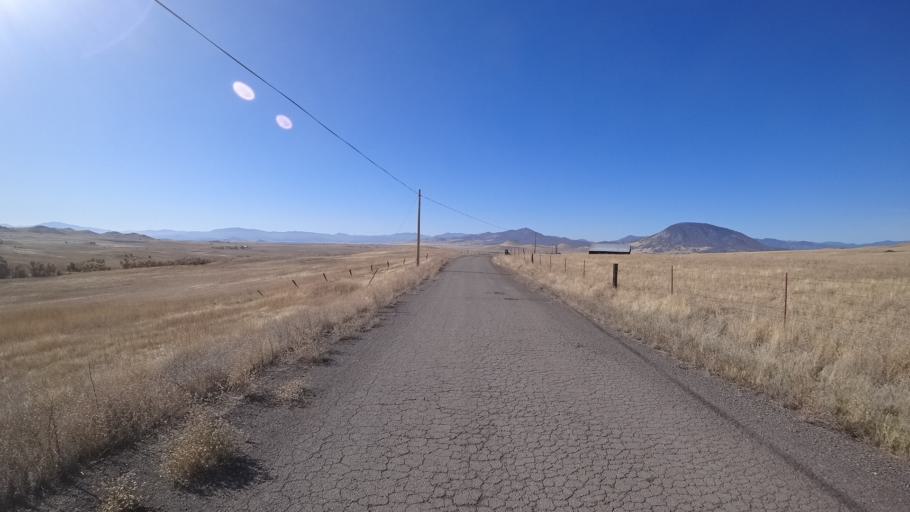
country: US
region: California
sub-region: Siskiyou County
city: Montague
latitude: 41.8299
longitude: -122.3939
